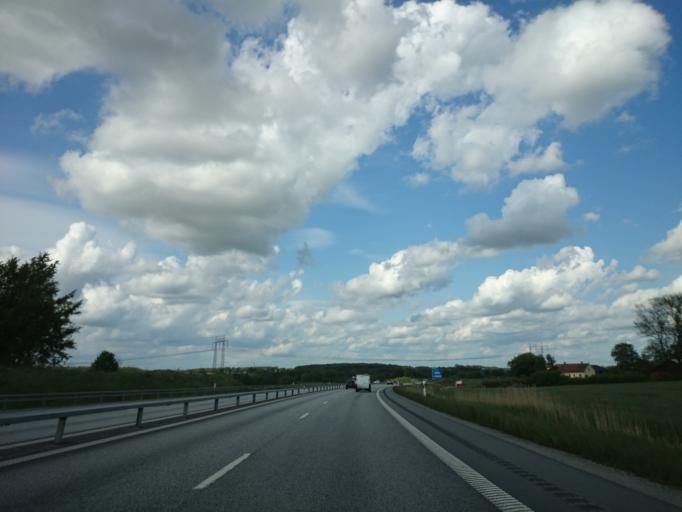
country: SE
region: Skane
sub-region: Hoors Kommun
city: Loberod
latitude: 55.8002
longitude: 13.4508
